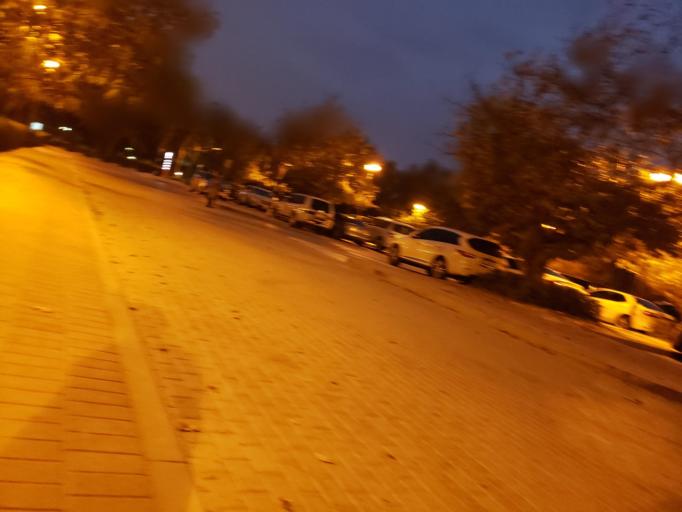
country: AE
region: Ash Shariqah
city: Sharjah
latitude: 25.3219
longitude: 55.3519
